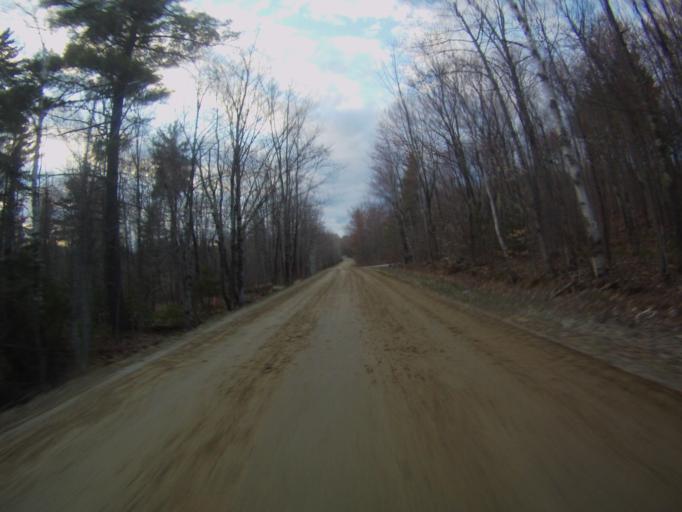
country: US
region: Vermont
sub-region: Rutland County
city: Brandon
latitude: 43.9049
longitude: -73.0163
